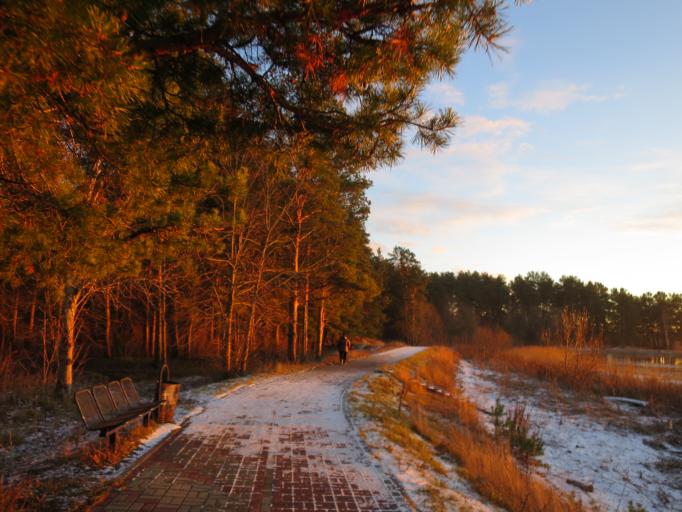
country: LV
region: Riga
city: Bergi
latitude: 56.9767
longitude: 24.3057
